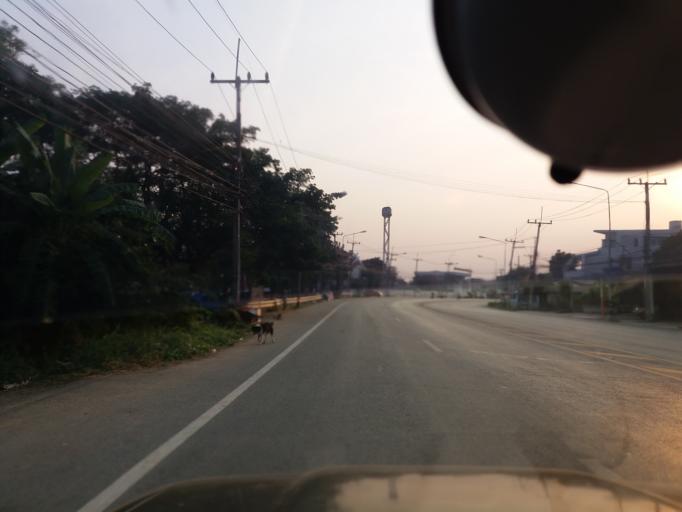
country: TH
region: Sing Buri
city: Sing Buri
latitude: 14.8890
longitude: 100.3972
